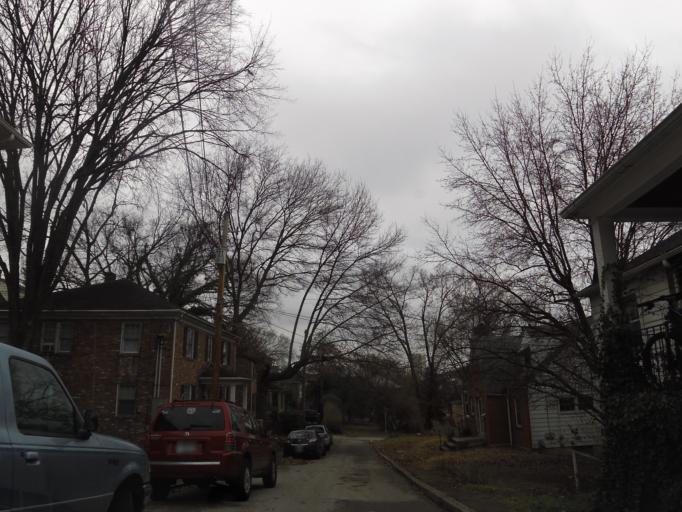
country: US
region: Kentucky
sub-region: Franklin County
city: Frankfort
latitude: 38.1915
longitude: -84.8808
